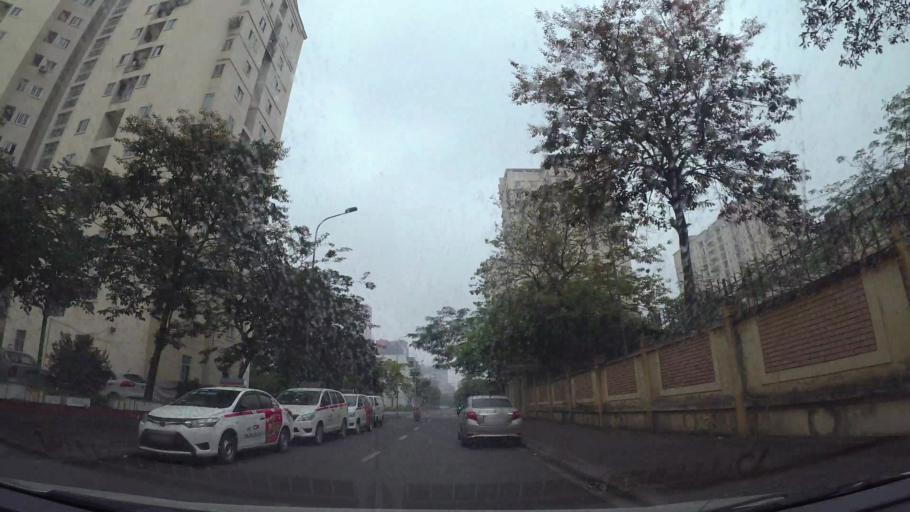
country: VN
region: Ha Noi
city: Cau Giay
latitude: 21.0144
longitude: 105.7879
